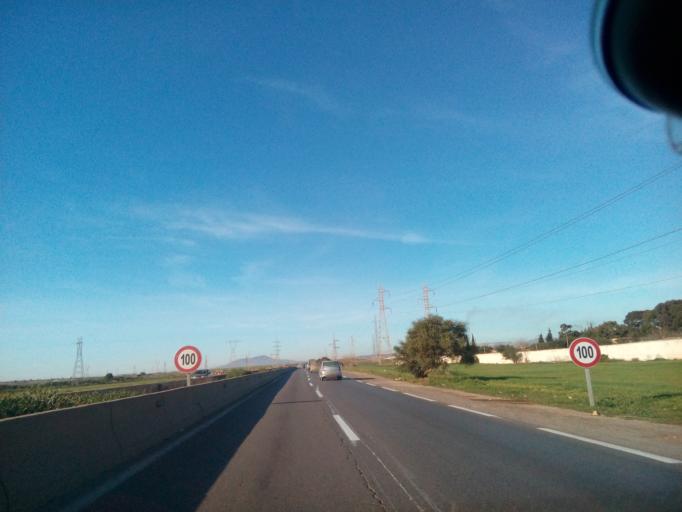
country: DZ
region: Oran
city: Ain el Bya
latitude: 35.8017
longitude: -0.3052
